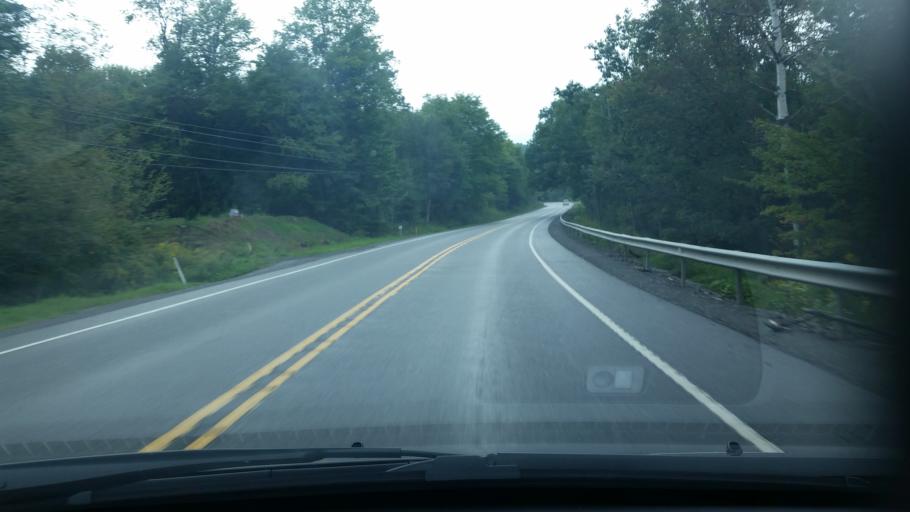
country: US
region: Pennsylvania
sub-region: Clearfield County
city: Shiloh
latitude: 41.0854
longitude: -78.2569
